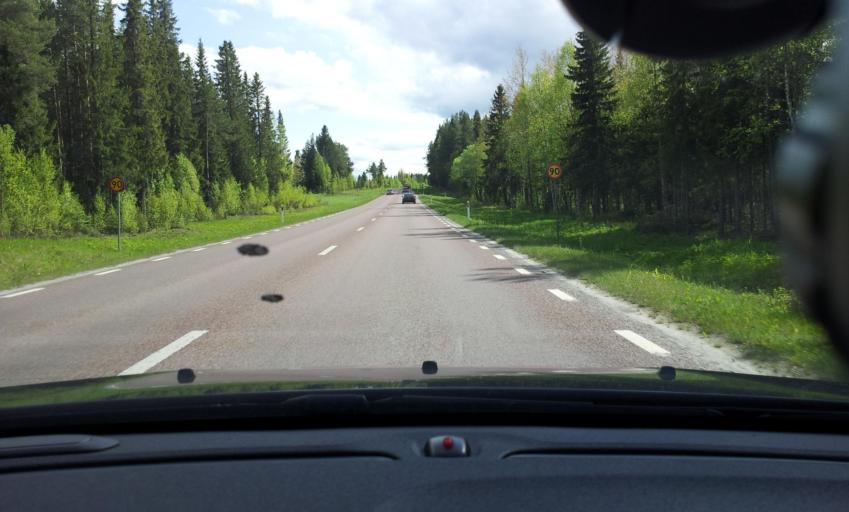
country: SE
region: Jaemtland
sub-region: OEstersunds Kommun
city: Brunflo
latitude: 63.0631
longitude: 14.8354
